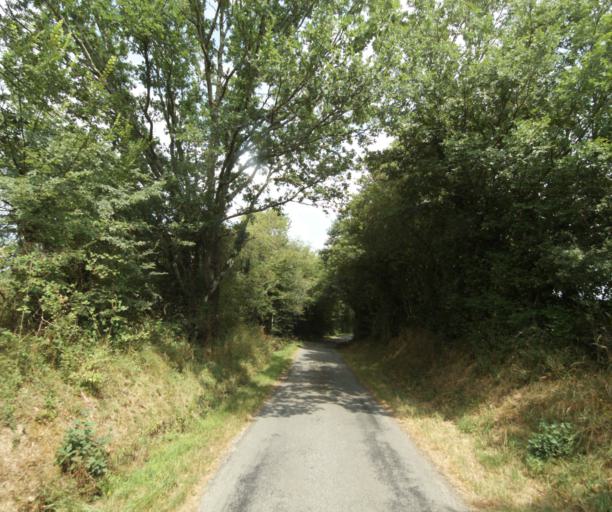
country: FR
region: Bourgogne
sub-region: Departement de Saone-et-Loire
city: Gueugnon
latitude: 46.5806
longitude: 4.0415
